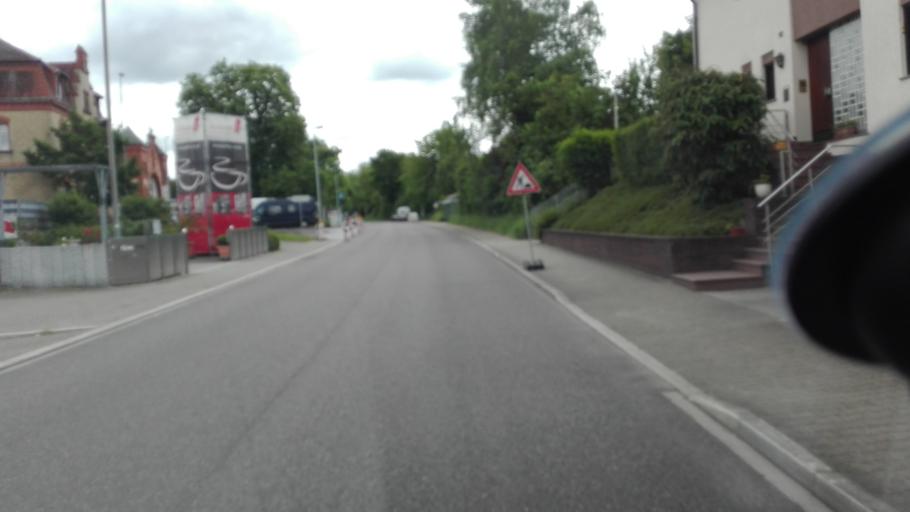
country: DE
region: Baden-Wuerttemberg
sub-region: Karlsruhe Region
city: Bruchsal
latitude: 49.1194
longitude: 8.6094
